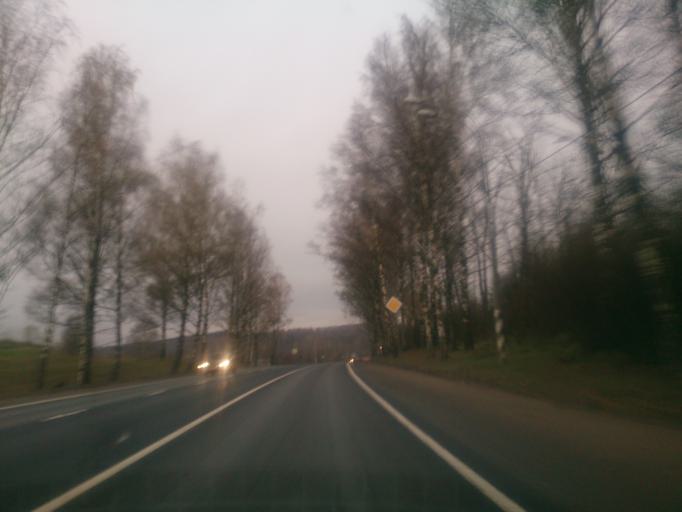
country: RU
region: Novgorod
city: Valday
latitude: 58.0365
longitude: 32.9660
